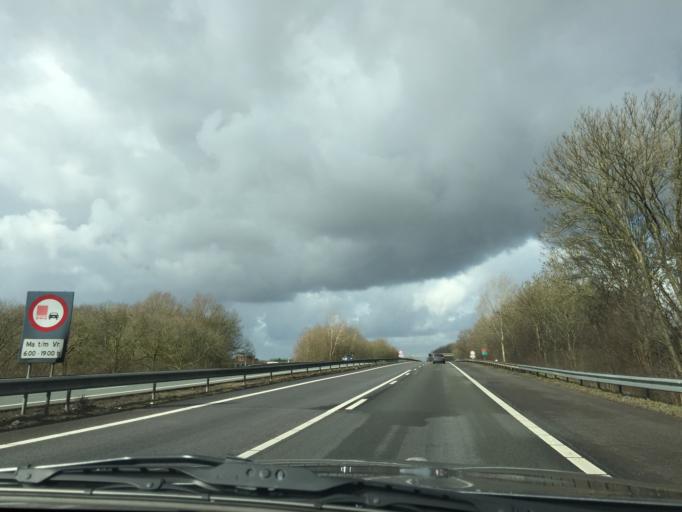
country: NL
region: Gelderland
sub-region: Gemeente Zevenaar
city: Zevenaar
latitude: 51.9408
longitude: 6.0857
